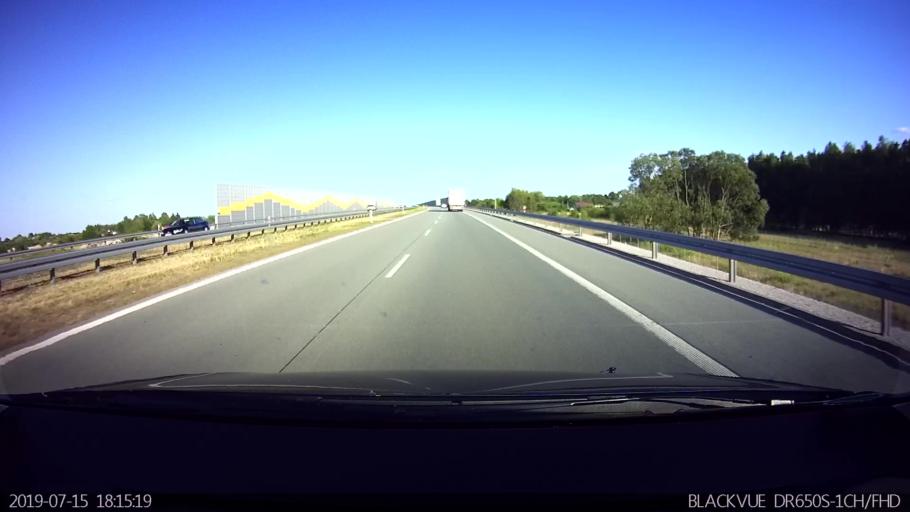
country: PL
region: Lodz Voivodeship
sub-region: Powiat zdunskowolski
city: Zdunska Wola
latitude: 51.5814
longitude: 18.9067
